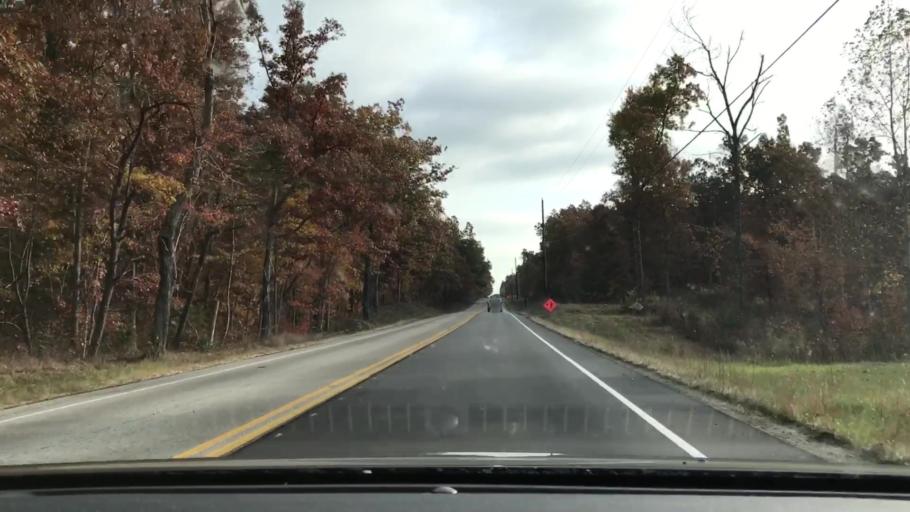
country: US
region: Tennessee
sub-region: Putnam County
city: Monterey
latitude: 36.1257
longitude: -85.1554
